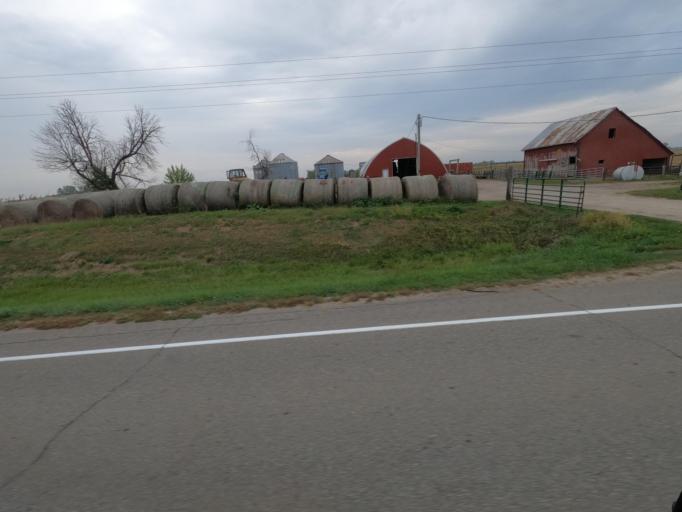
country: US
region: Iowa
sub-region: Van Buren County
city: Keosauqua
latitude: 40.8133
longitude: -91.7518
